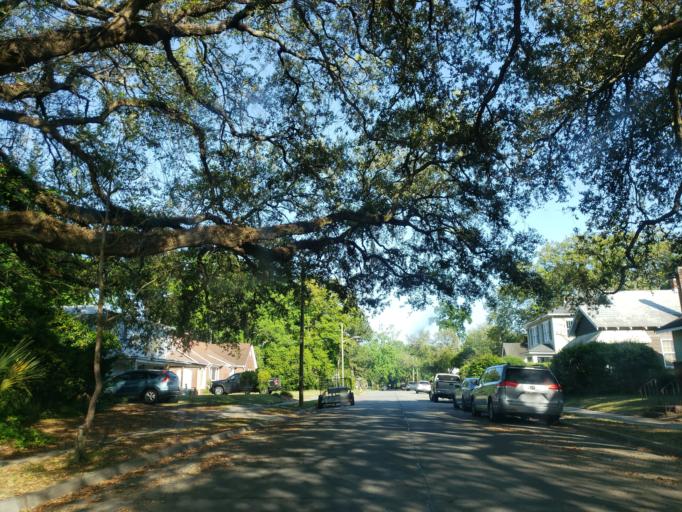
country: US
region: Georgia
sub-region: Chatham County
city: Thunderbolt
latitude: 32.0405
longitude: -81.0815
